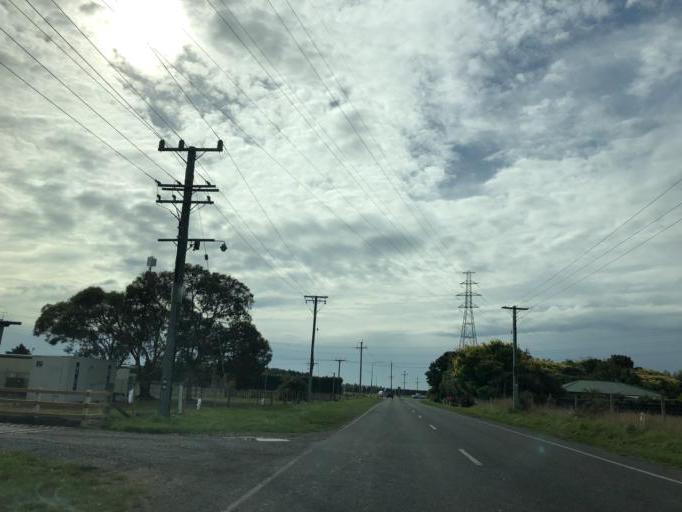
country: NZ
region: Canterbury
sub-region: Selwyn District
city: Lincoln
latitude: -43.6376
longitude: 172.4508
